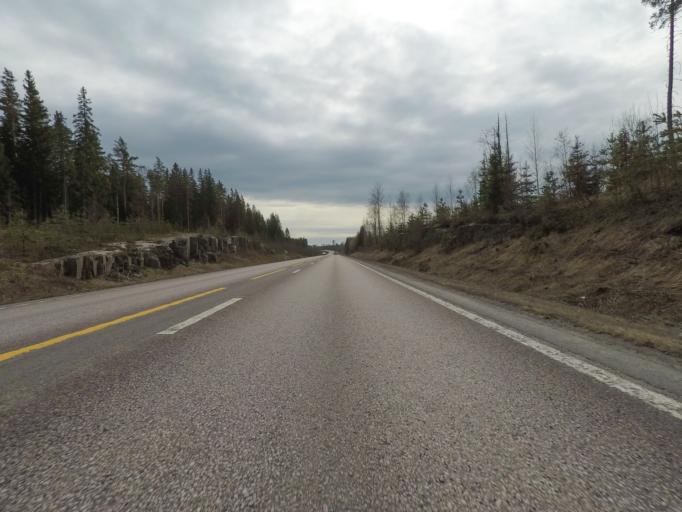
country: FI
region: Paijanne Tavastia
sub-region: Lahti
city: Heinola
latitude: 61.3836
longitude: 26.0515
